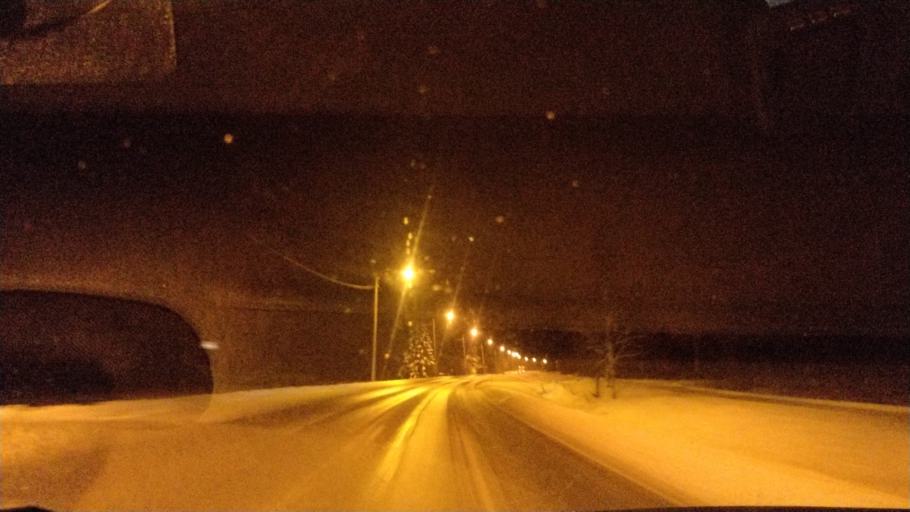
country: FI
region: Lapland
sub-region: Rovaniemi
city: Rovaniemi
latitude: 66.3162
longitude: 25.3617
